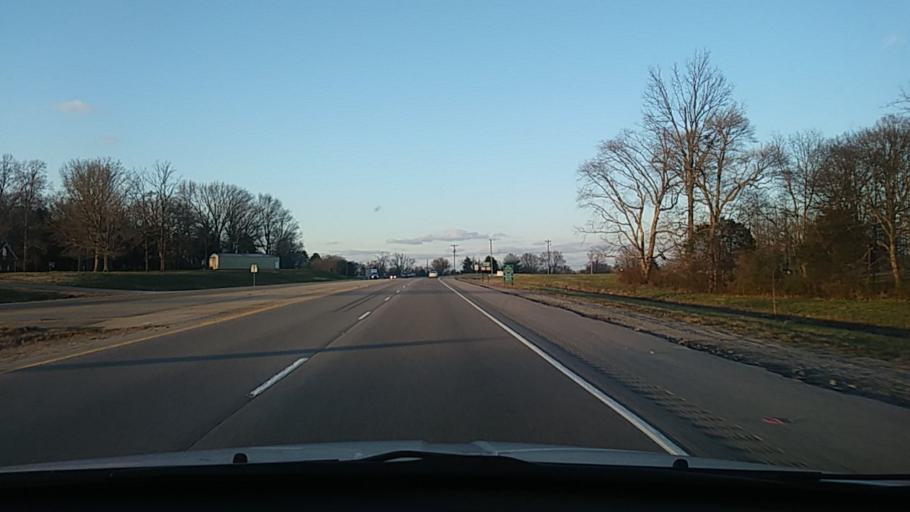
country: US
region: Tennessee
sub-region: Sumner County
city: Portland
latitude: 36.5407
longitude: -86.5066
